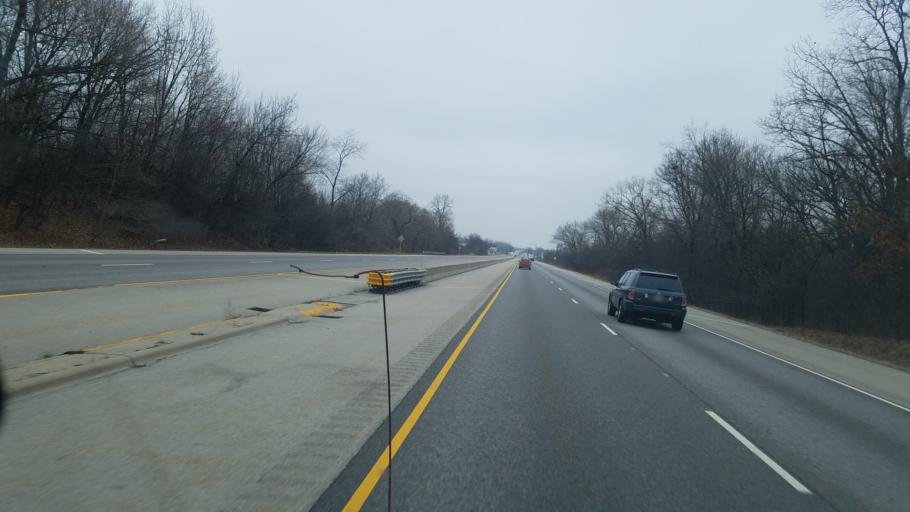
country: US
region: Illinois
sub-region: Lake County
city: Wadsworth
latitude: 42.4576
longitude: -87.9459
